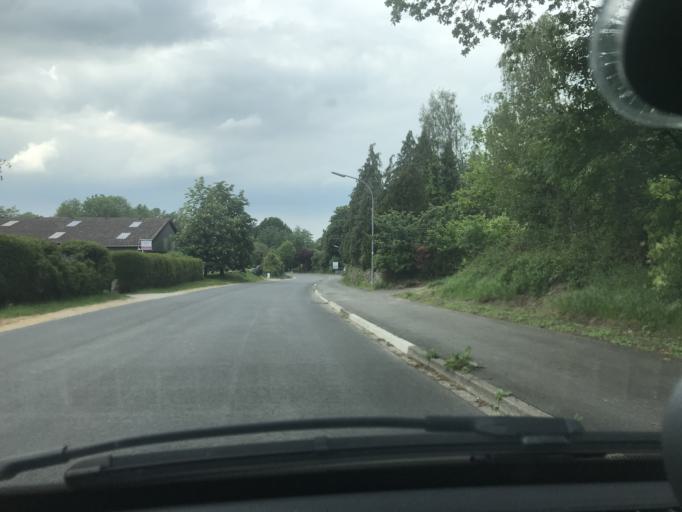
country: DE
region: Schleswig-Holstein
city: Rausdorf
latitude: 53.5873
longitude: 10.3320
